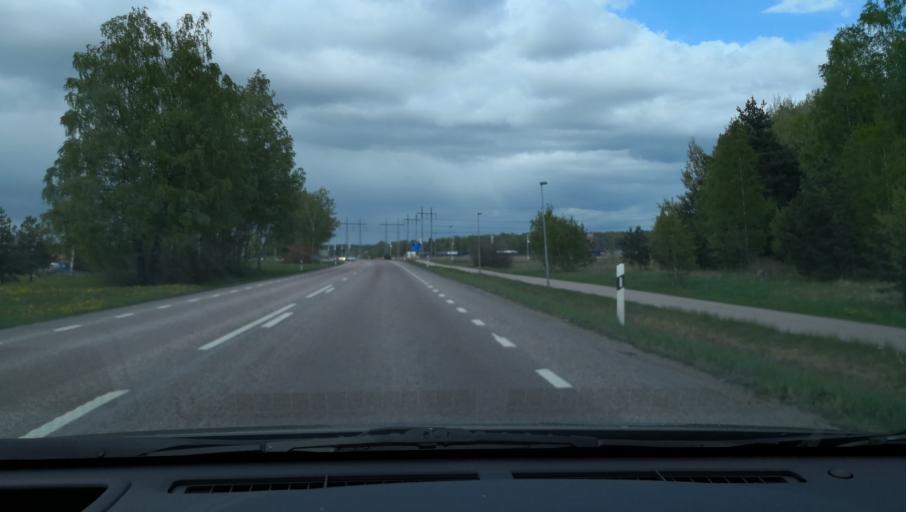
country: SE
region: Vaestmanland
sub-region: Vasteras
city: Hokasen
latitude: 59.6466
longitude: 16.5730
